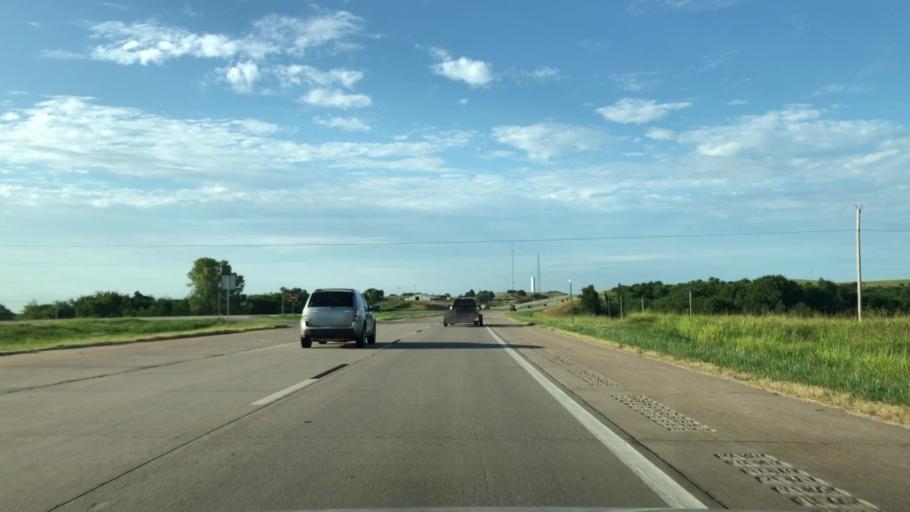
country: US
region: Oklahoma
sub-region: Osage County
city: Skiatook
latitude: 36.5112
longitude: -95.9214
